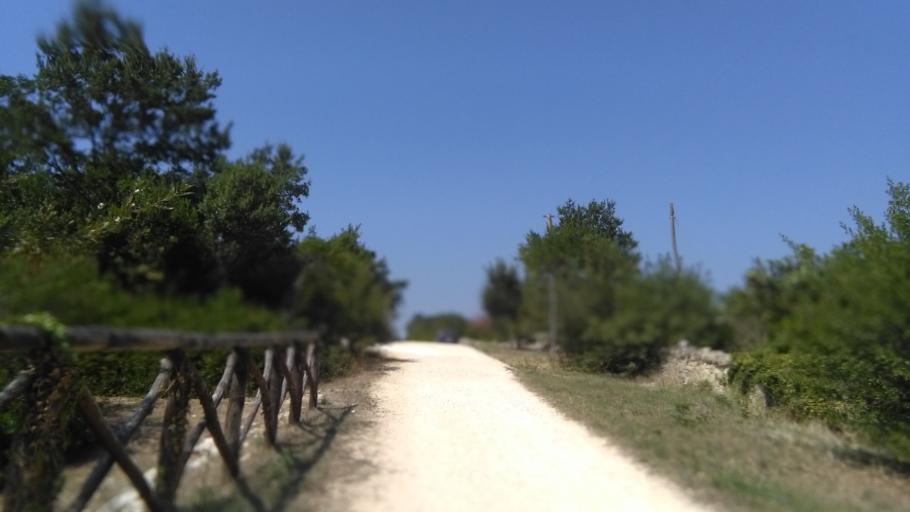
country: IT
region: Apulia
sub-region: Provincia di Brindisi
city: Cisternino
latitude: 40.6887
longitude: 17.4293
